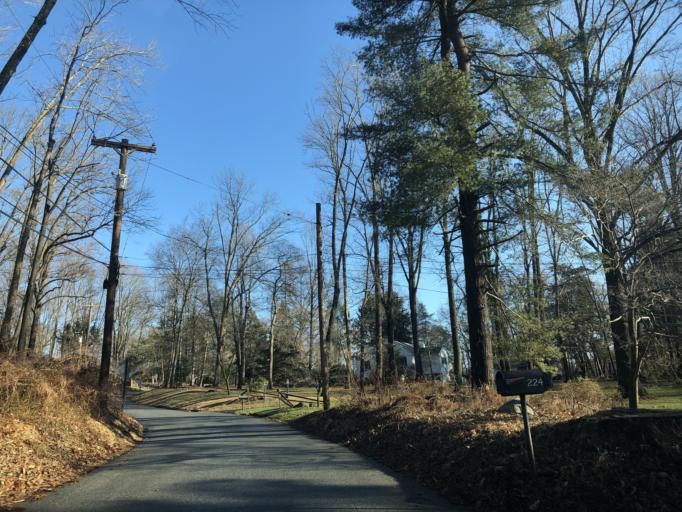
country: US
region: Pennsylvania
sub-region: Delaware County
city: Chester Heights
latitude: 39.9331
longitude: -75.4911
